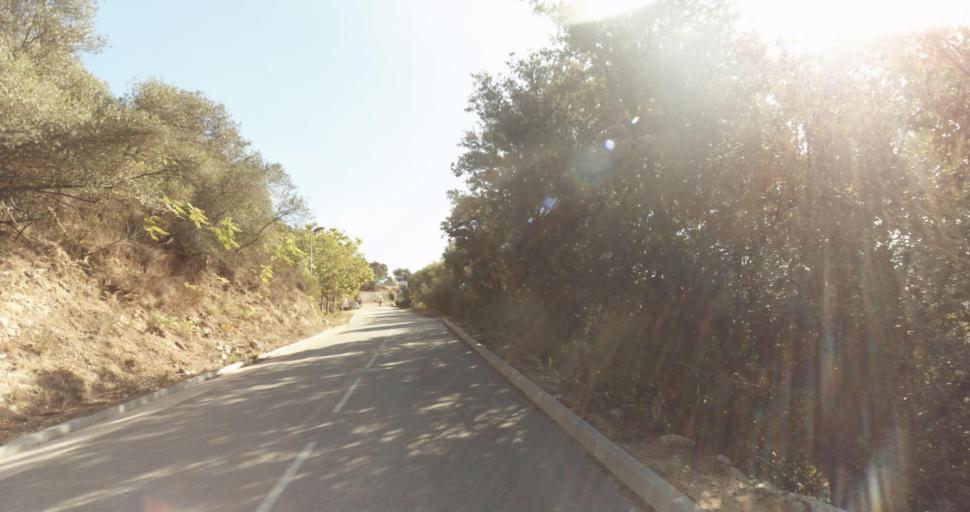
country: FR
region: Corsica
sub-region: Departement de la Corse-du-Sud
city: Ajaccio
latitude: 41.9335
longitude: 8.7090
